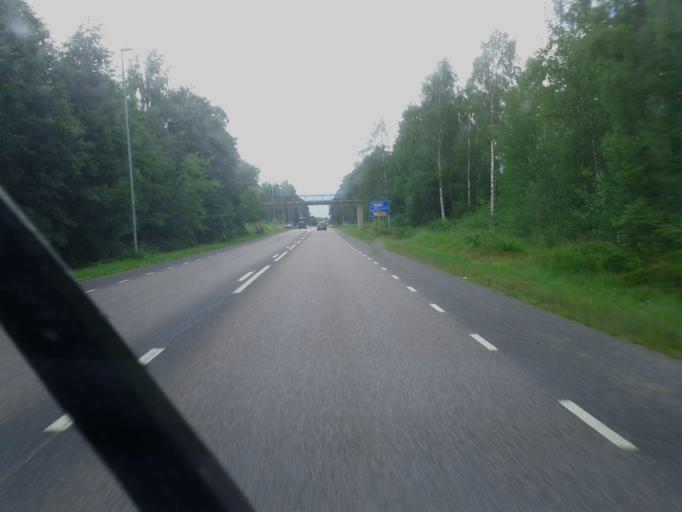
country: SE
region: Vaestmanland
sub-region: Sala Kommun
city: Sala
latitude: 59.9131
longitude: 16.5869
